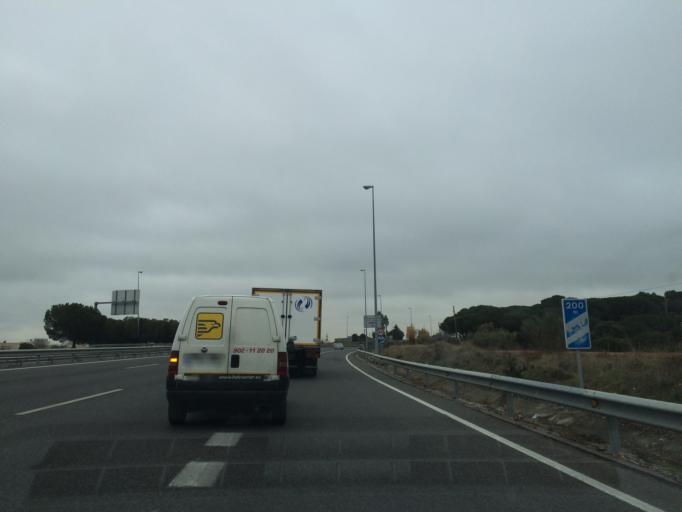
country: ES
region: Madrid
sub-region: Provincia de Madrid
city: Tres Cantos
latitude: 40.5957
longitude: -3.7153
